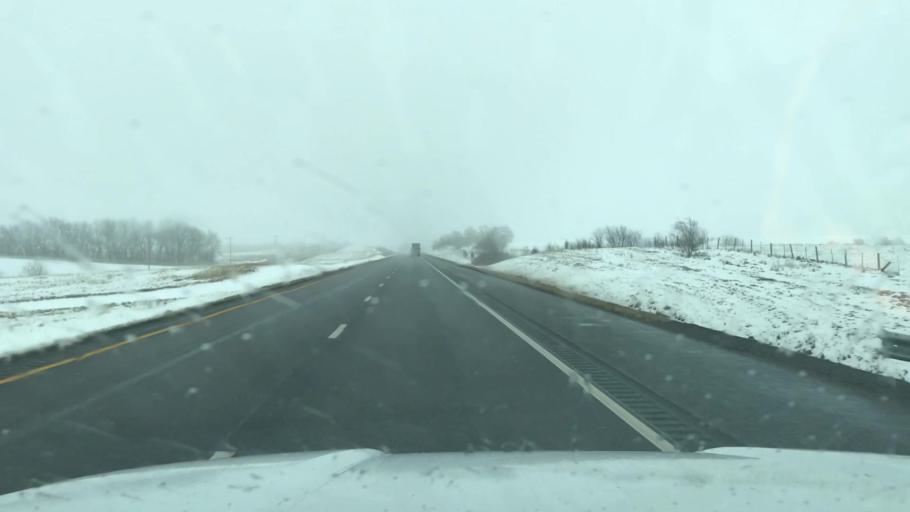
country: US
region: Missouri
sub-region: Clinton County
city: Gower
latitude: 39.7618
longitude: -94.5347
